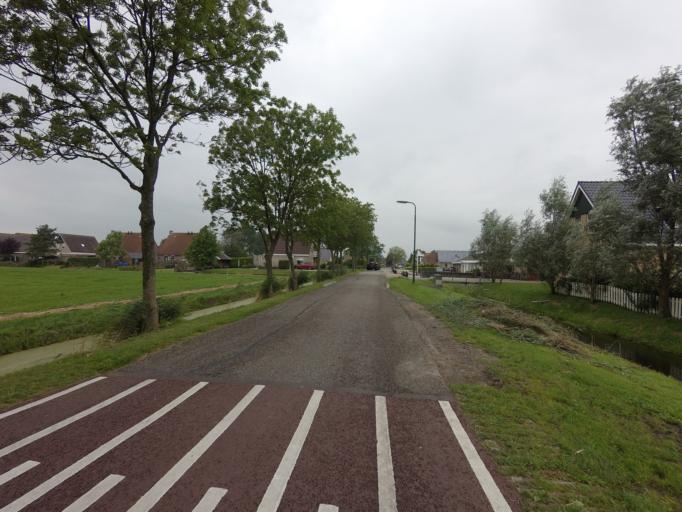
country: NL
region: Friesland
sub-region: Sudwest Fryslan
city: Workum
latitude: 53.0166
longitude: 5.4830
